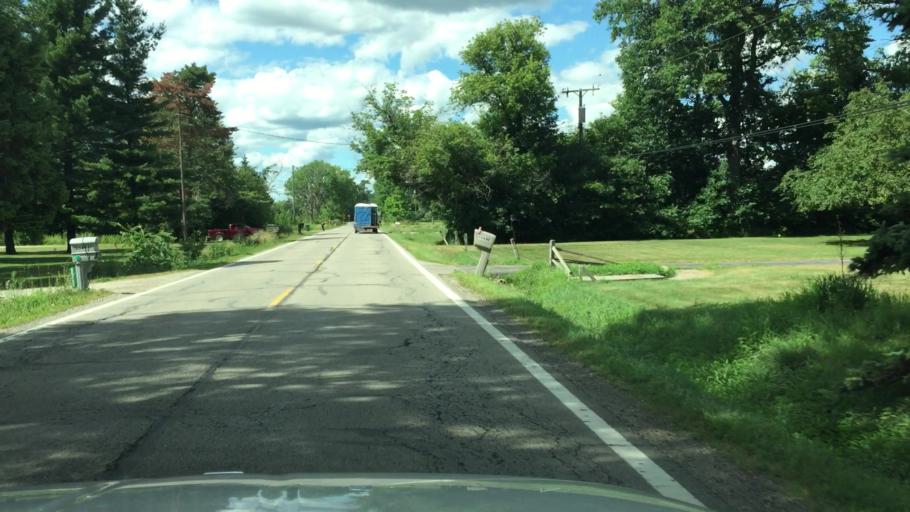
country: US
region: Michigan
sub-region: Macomb County
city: Armada
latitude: 42.8894
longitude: -82.9457
